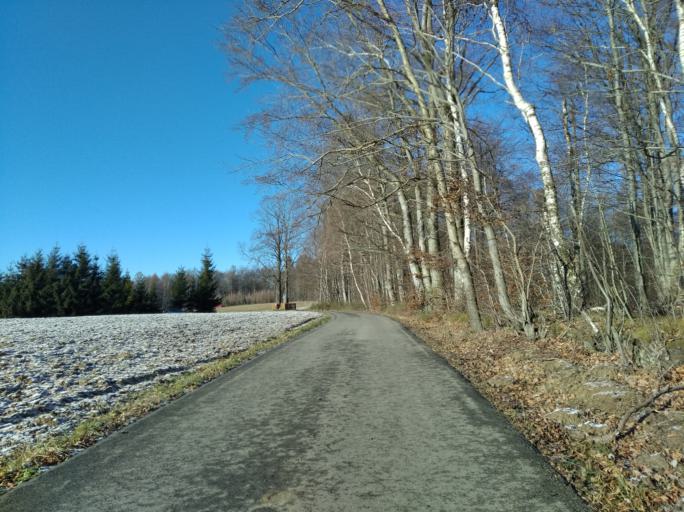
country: PL
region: Subcarpathian Voivodeship
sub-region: Powiat ropczycko-sedziszowski
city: Iwierzyce
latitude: 49.9684
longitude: 21.7335
